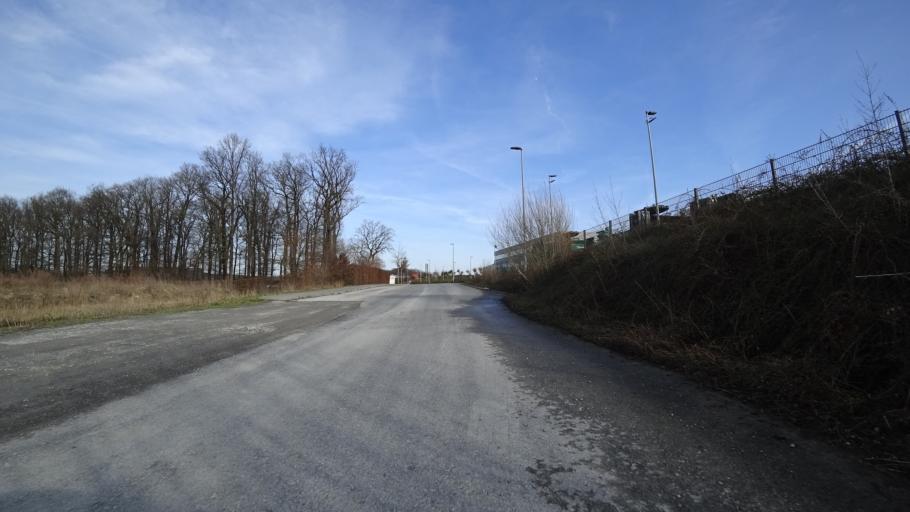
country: DE
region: North Rhine-Westphalia
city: Oelde
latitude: 51.8114
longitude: 8.1161
